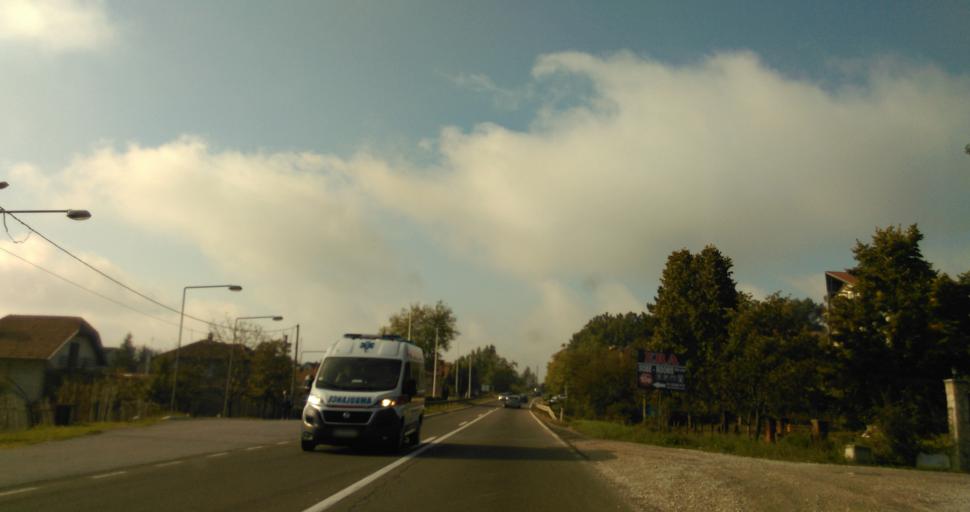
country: RS
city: Vranic
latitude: 44.6194
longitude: 20.3666
